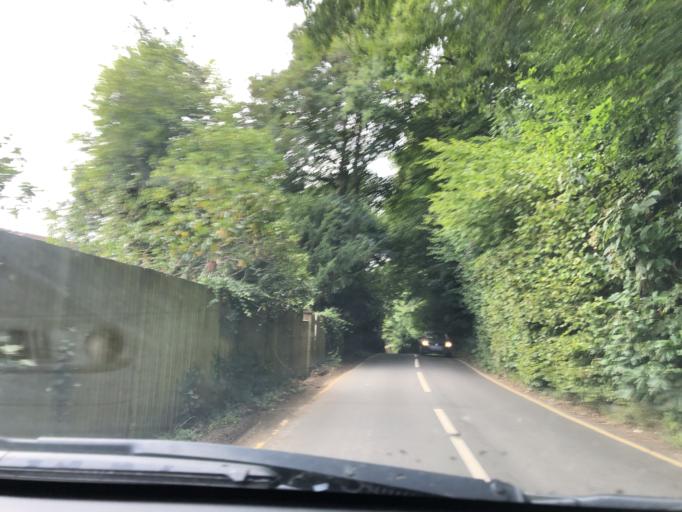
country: GB
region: England
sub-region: Kent
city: Westerham
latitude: 51.2435
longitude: 0.0820
